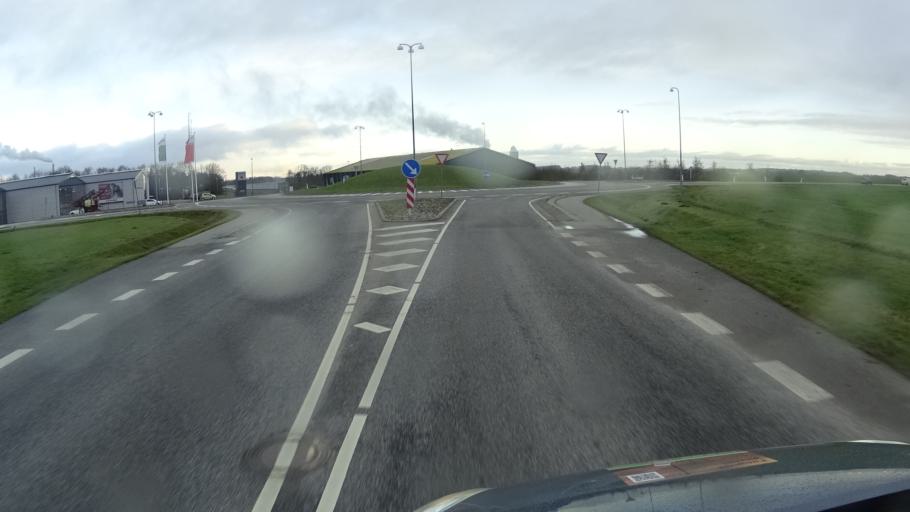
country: DK
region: South Denmark
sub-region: Vejle Kommune
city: Jelling
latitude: 55.7571
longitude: 9.4399
